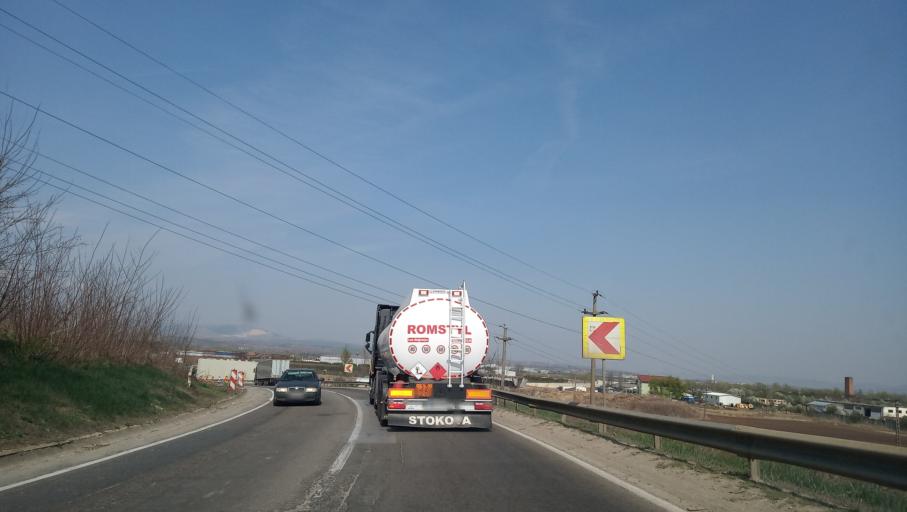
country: RO
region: Alba
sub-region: Comuna Santimbru
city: Santimbru
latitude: 46.1465
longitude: 23.6453
